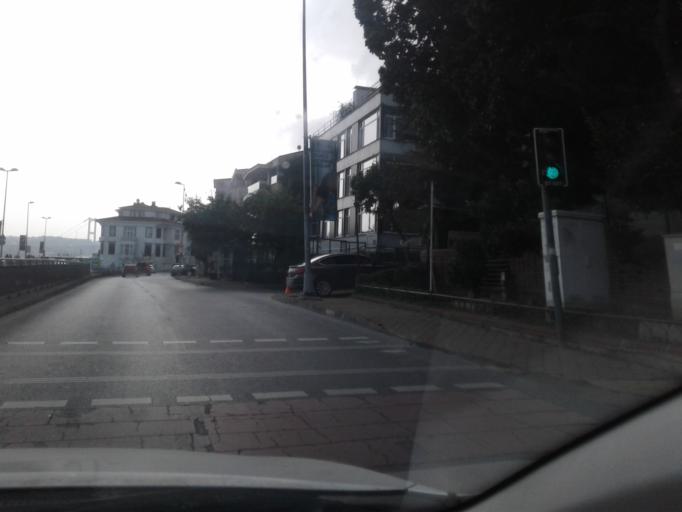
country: TR
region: Istanbul
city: UEskuedar
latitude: 41.0644
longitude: 29.0408
